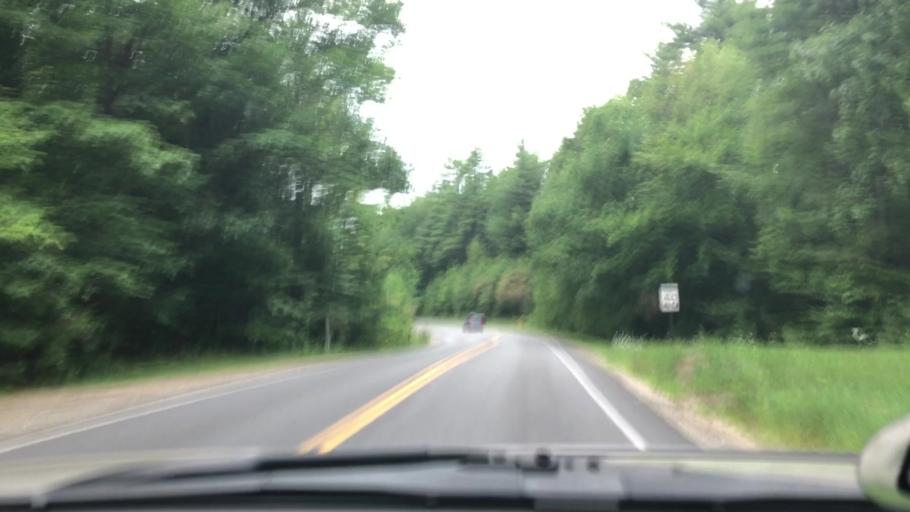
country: US
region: New York
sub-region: Saratoga County
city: Corinth
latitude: 43.2011
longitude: -73.7652
